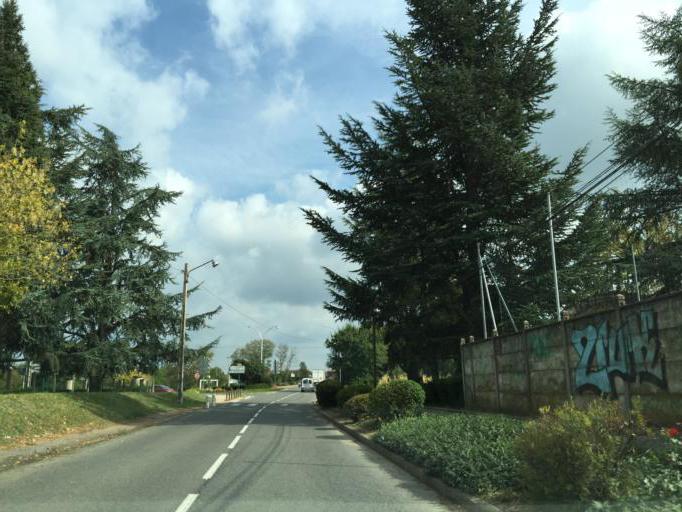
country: FR
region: Rhone-Alpes
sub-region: Departement de la Loire
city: Sury-le-Comtal
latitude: 45.5419
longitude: 4.1766
